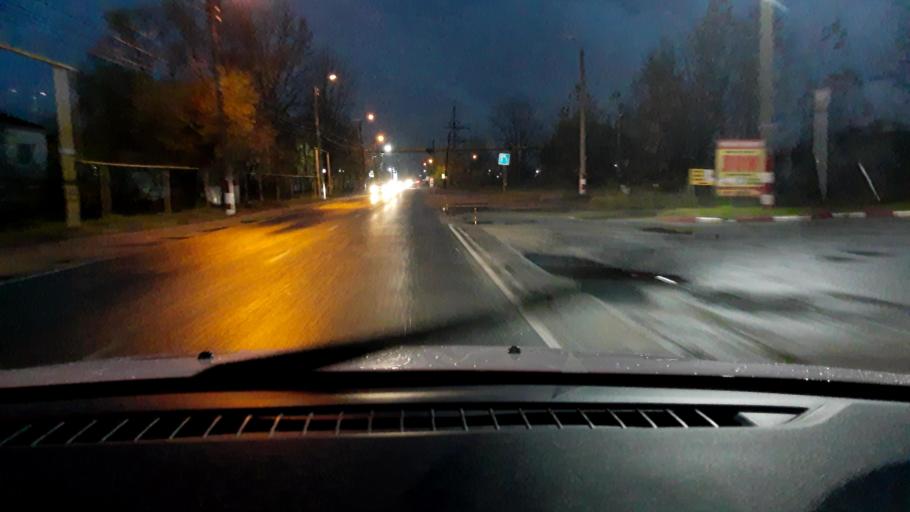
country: RU
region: Nizjnij Novgorod
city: Bor
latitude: 56.3534
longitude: 44.0916
